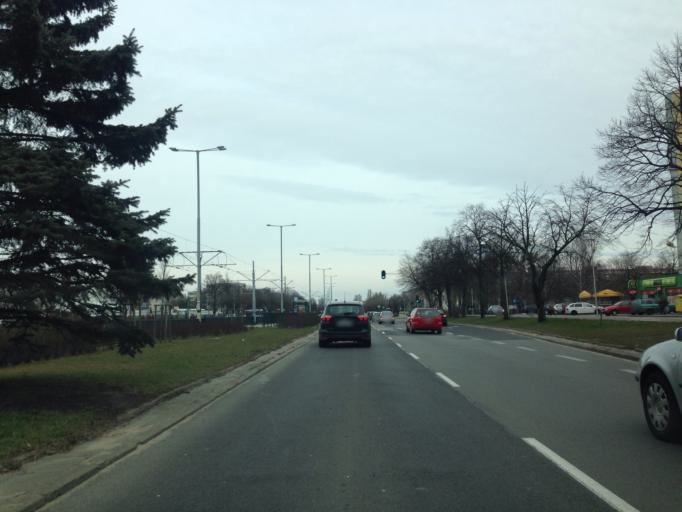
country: PL
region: Pomeranian Voivodeship
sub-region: Sopot
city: Sopot
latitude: 54.4108
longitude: 18.5884
